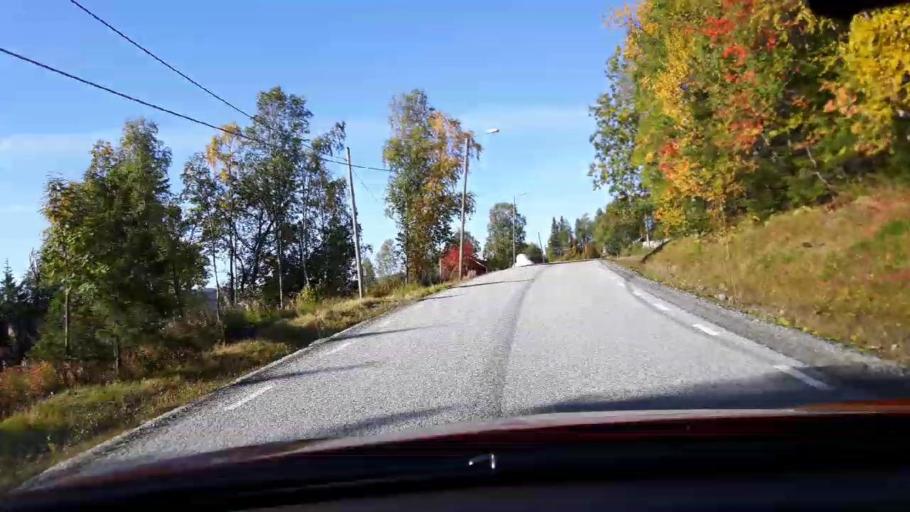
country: NO
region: Nord-Trondelag
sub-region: Royrvik
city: Royrvik
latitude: 64.8288
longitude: 14.1209
